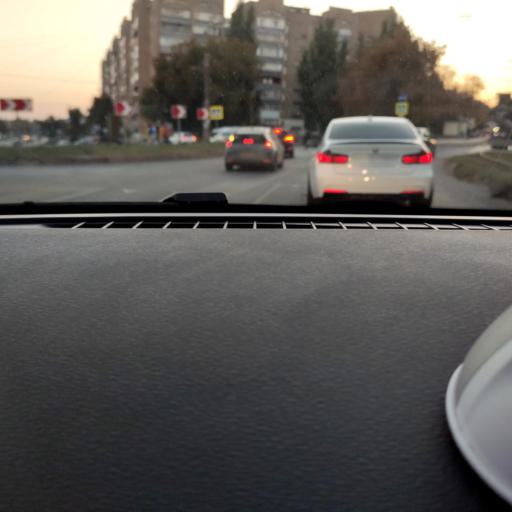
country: RU
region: Samara
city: Samara
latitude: 53.1922
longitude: 50.2135
